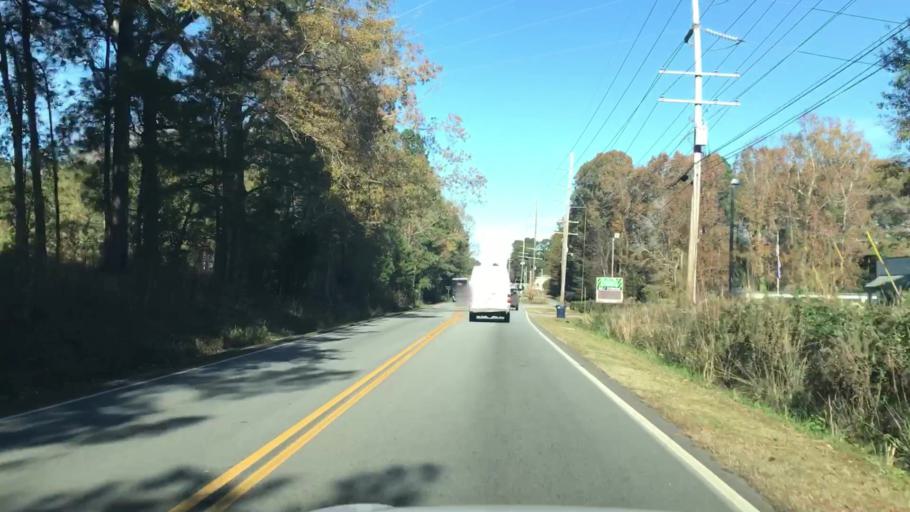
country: US
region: South Carolina
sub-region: Dorchester County
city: Centerville
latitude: 32.9872
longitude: -80.2213
